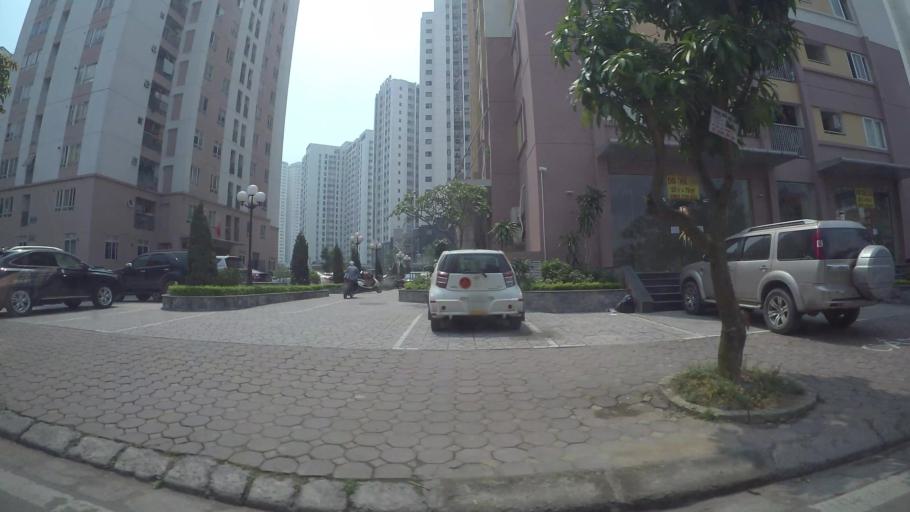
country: VN
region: Ha Noi
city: Van Dien
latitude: 20.9650
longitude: 105.8224
